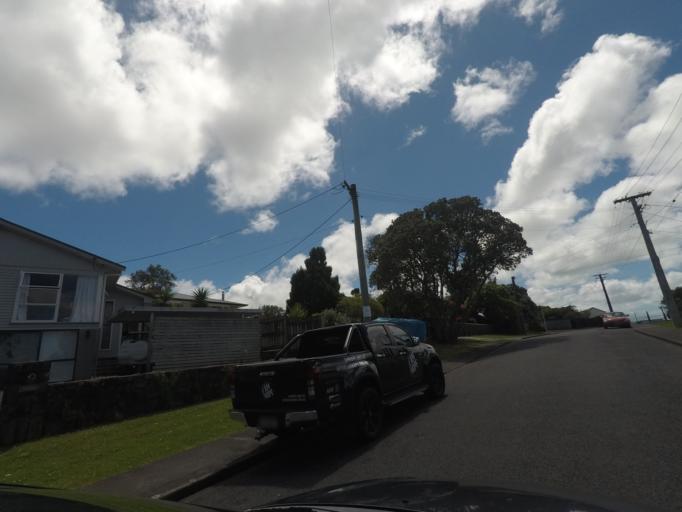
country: NZ
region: Auckland
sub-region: Auckland
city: Rosebank
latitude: -36.8712
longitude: 174.6493
